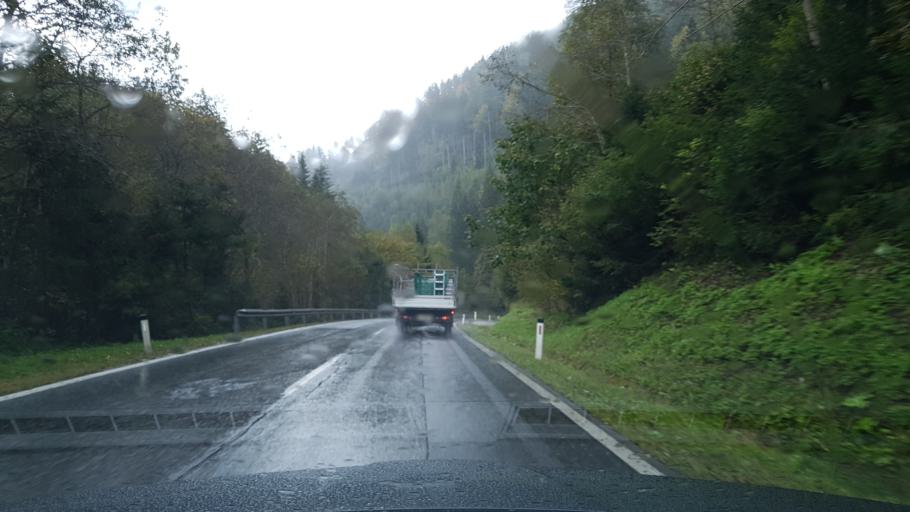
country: AT
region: Styria
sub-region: Politischer Bezirk Voitsberg
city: Salla
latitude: 47.1042
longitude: 14.9490
